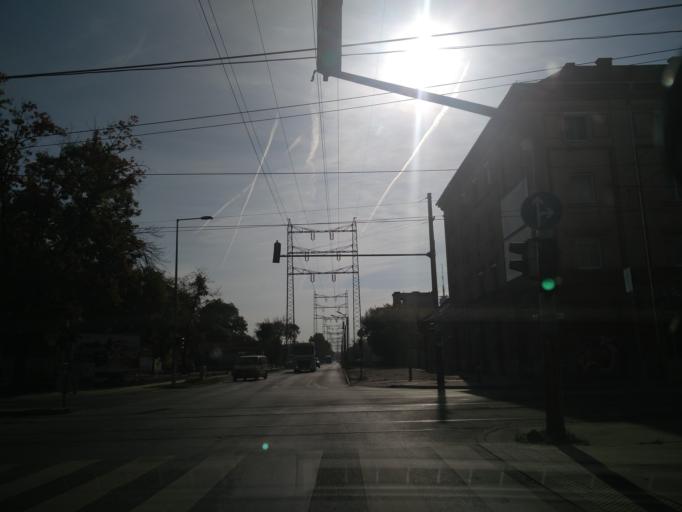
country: HU
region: Budapest
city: Budapest XIX. keruelet
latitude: 47.4760
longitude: 19.1189
